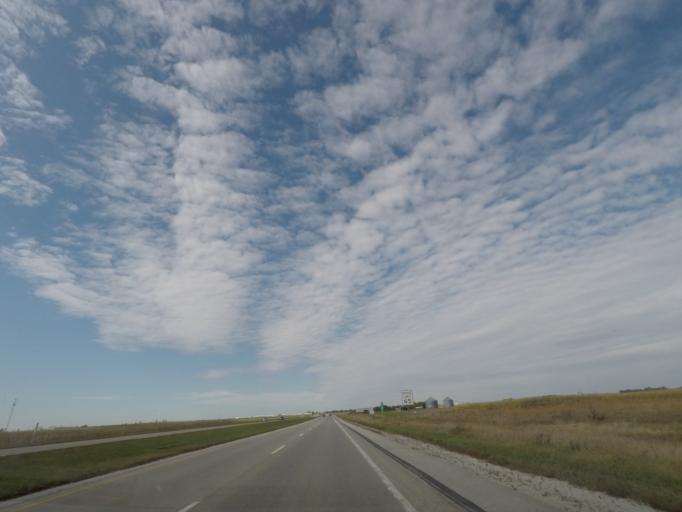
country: US
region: Iowa
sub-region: Story County
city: Ames
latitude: 42.0234
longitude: -93.7481
